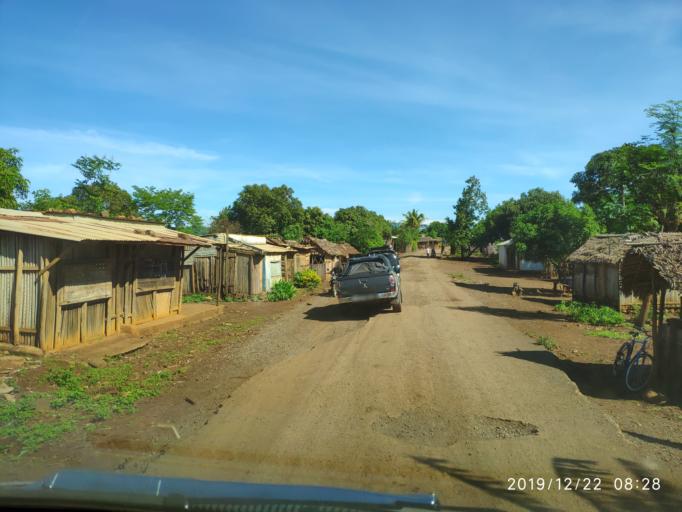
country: MG
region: Diana
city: Sadjoavato
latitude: -12.9004
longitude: 49.2123
